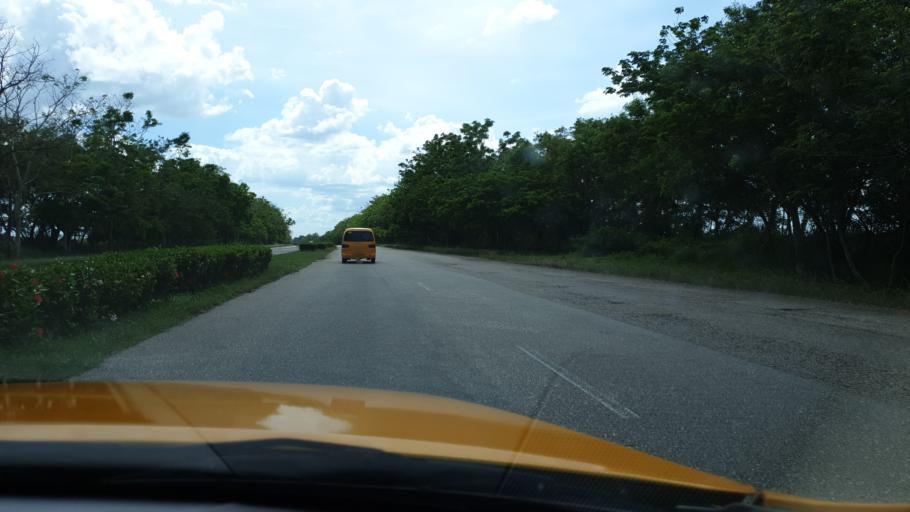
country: CU
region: Cienfuegos
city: Cruces
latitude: 22.4553
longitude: -80.3076
